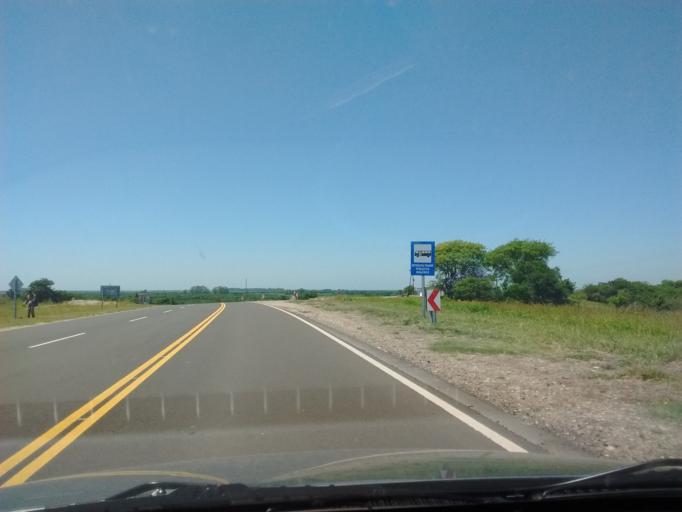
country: AR
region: Entre Rios
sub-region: Departamento de Victoria
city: Victoria
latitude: -32.8361
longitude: -59.8690
